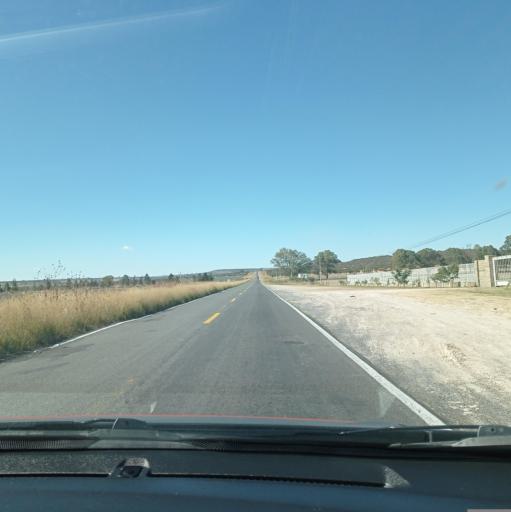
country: MX
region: Jalisco
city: San Diego de Alejandria
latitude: 21.0056
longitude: -102.0612
